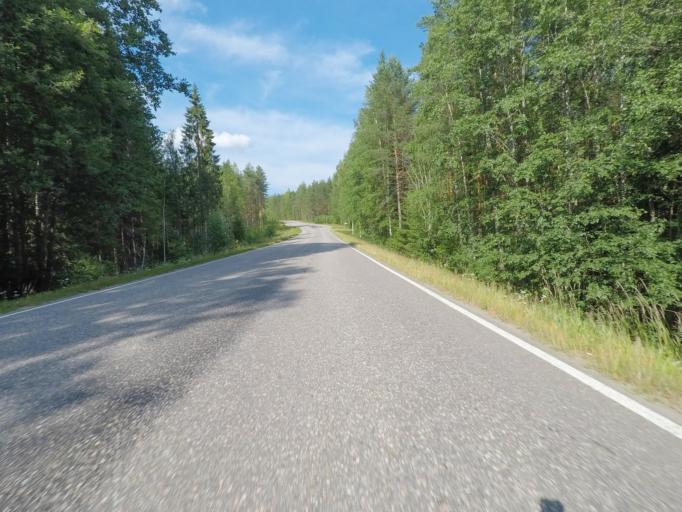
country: FI
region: Southern Savonia
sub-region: Mikkeli
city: Puumala
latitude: 61.6793
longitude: 28.2294
